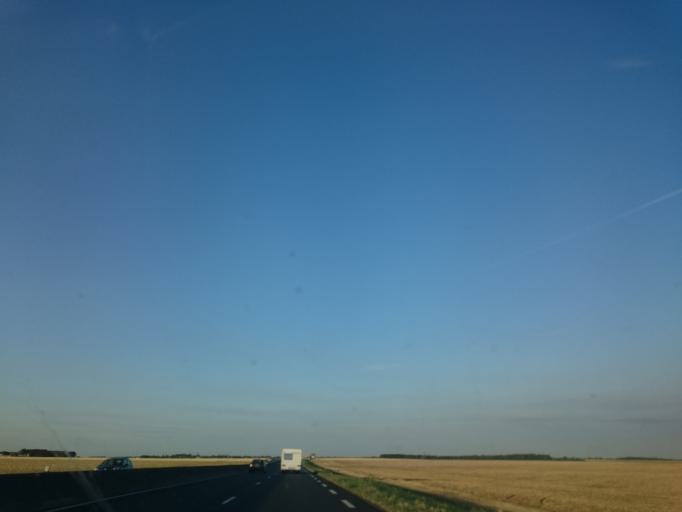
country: FR
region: Ile-de-France
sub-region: Departement de l'Essonne
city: Angerville
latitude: 48.3269
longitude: 2.0205
